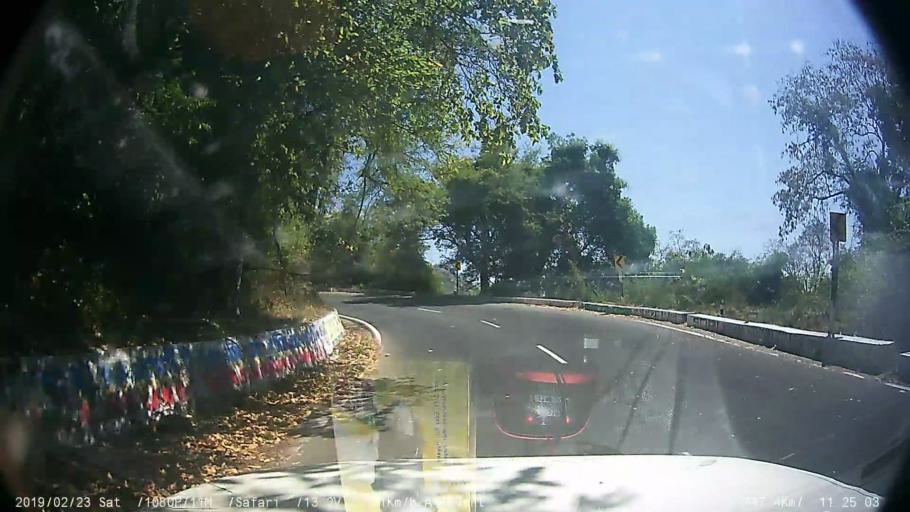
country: IN
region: Tamil Nadu
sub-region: Coimbatore
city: Mettupalayam
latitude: 11.3401
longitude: 76.8724
